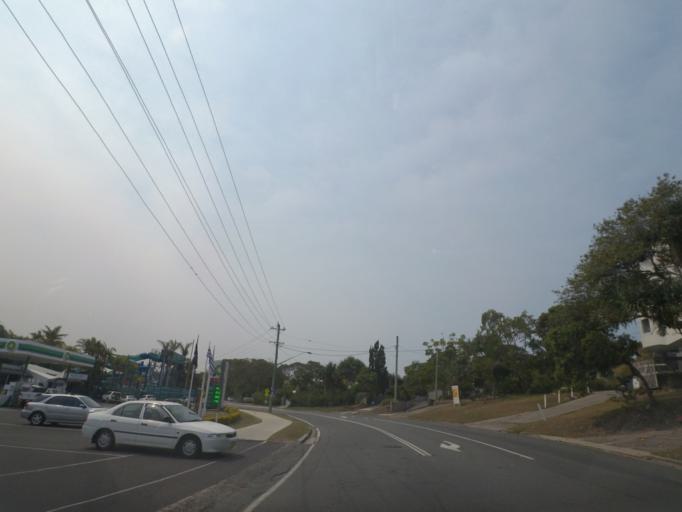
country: AU
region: New South Wales
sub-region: Tweed
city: Pottsville Beach
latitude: -28.3558
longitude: 153.5734
